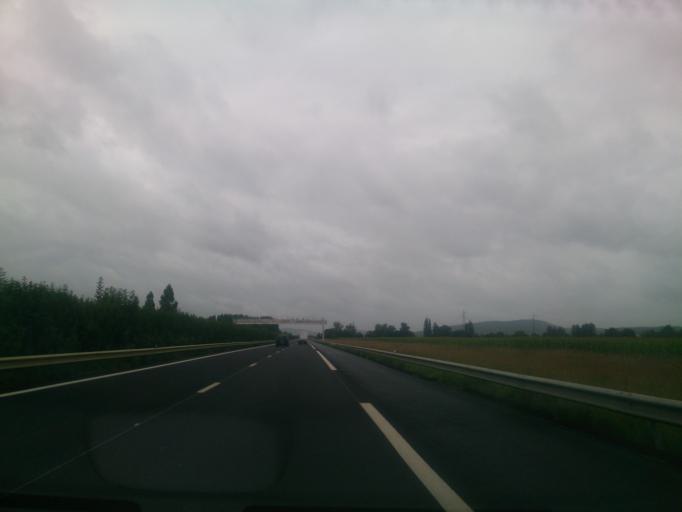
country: FR
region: Midi-Pyrenees
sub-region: Departement de la Haute-Garonne
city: Cazeres
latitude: 43.2237
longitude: 1.0523
